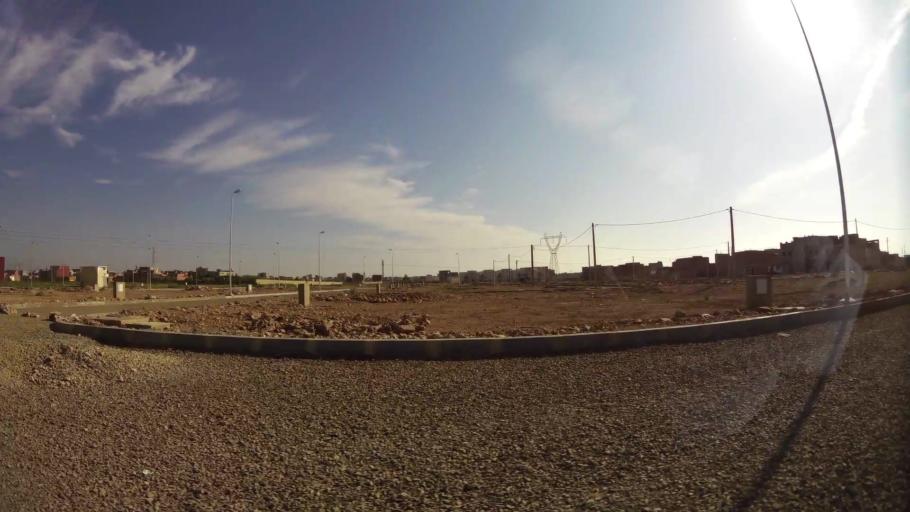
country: MA
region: Oriental
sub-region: Oujda-Angad
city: Oujda
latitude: 34.7246
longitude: -1.8855
